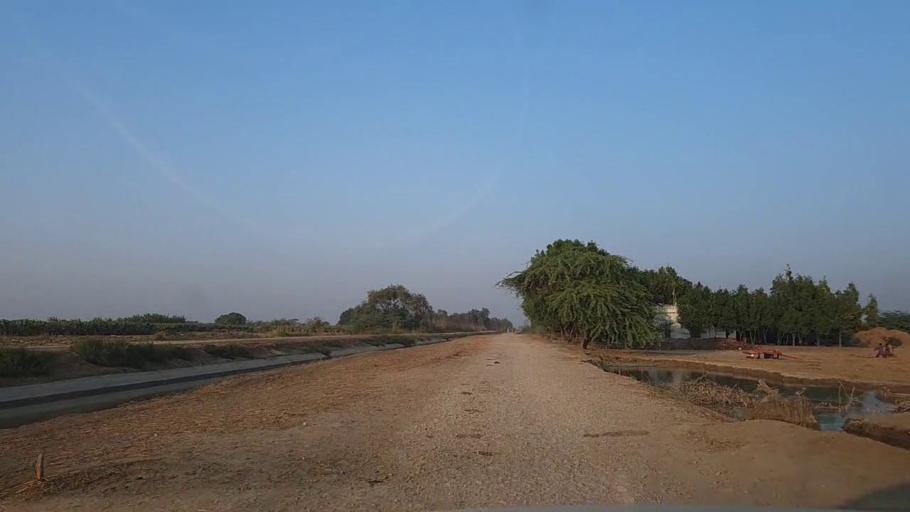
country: PK
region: Sindh
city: Mirpur Sakro
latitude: 24.2922
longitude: 67.6949
